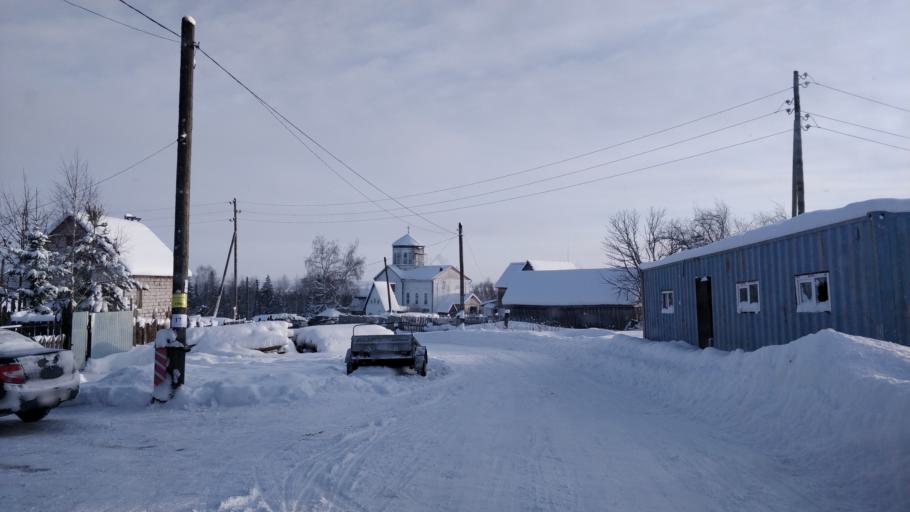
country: RU
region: Perm
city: Verkhnechusovskiye Gorodki
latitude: 58.2133
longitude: 57.0669
